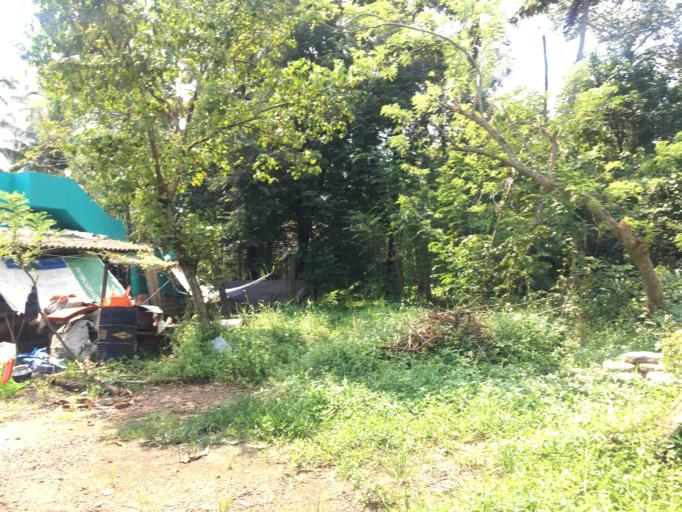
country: IN
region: Kerala
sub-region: Ernakulam
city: Cochin
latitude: 9.9660
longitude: 76.3233
